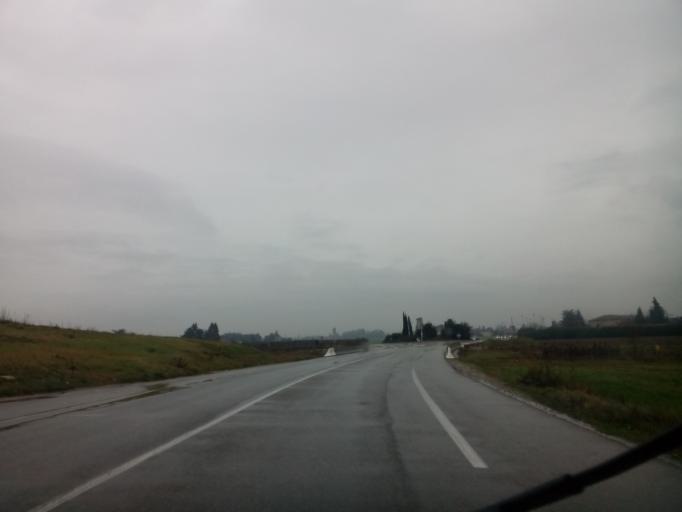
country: FR
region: Rhone-Alpes
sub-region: Departement de la Drome
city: Romans-sur-Isere
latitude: 45.0451
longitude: 5.0134
